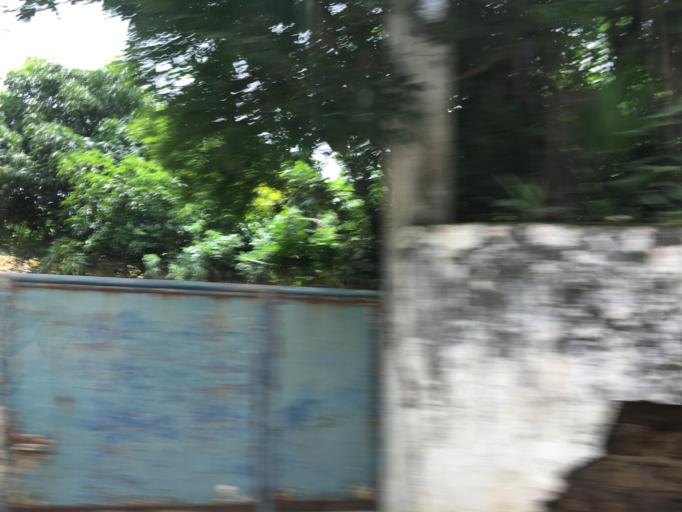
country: GT
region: Guatemala
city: Villa Canales
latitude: 14.4502
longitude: -90.5665
